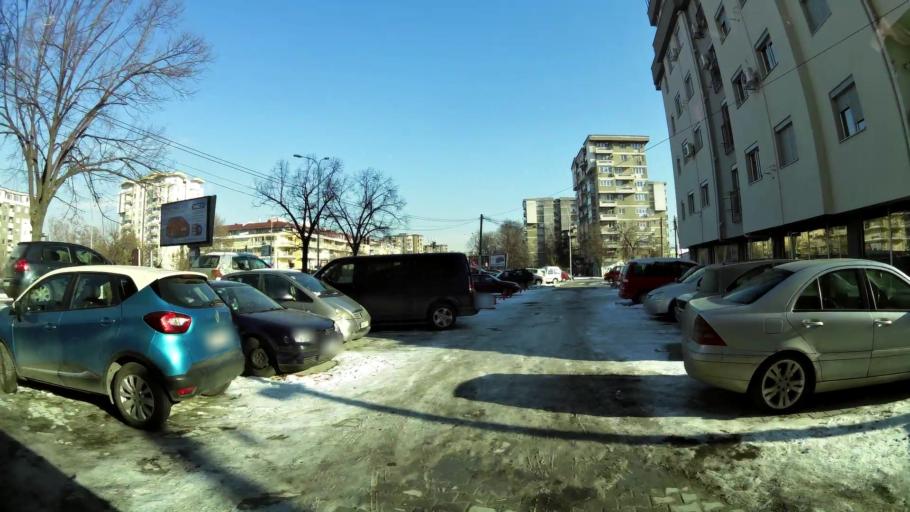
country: MK
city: Krushopek
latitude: 42.0047
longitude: 21.3818
